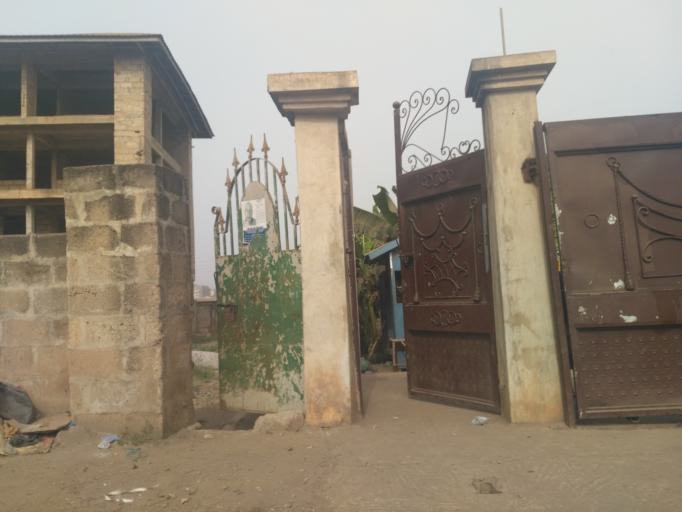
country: GH
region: Ashanti
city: Kumasi
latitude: 6.7043
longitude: -1.6321
